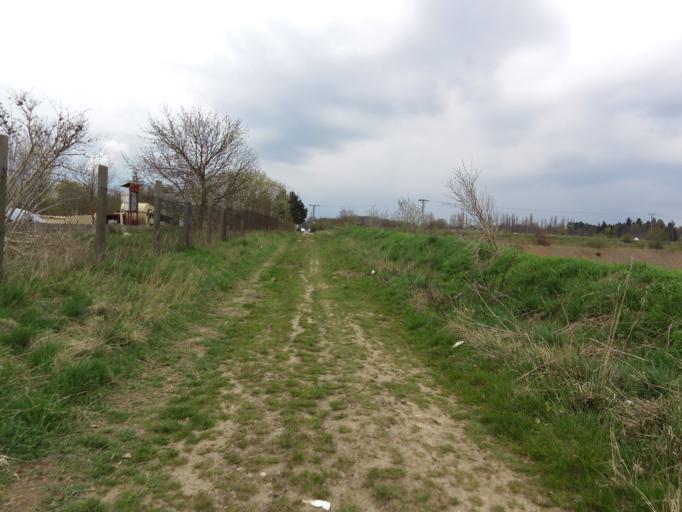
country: DE
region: Thuringia
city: Gotha
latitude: 50.9708
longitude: 10.7133
